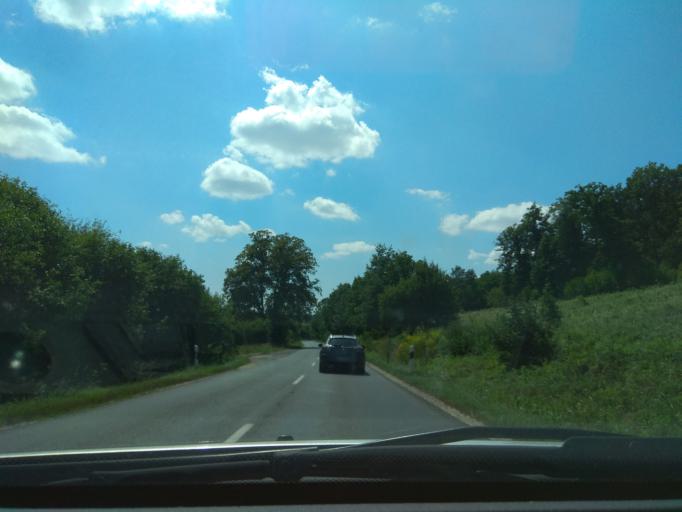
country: HU
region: Borsod-Abauj-Zemplen
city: Harsany
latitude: 48.0045
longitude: 20.7610
